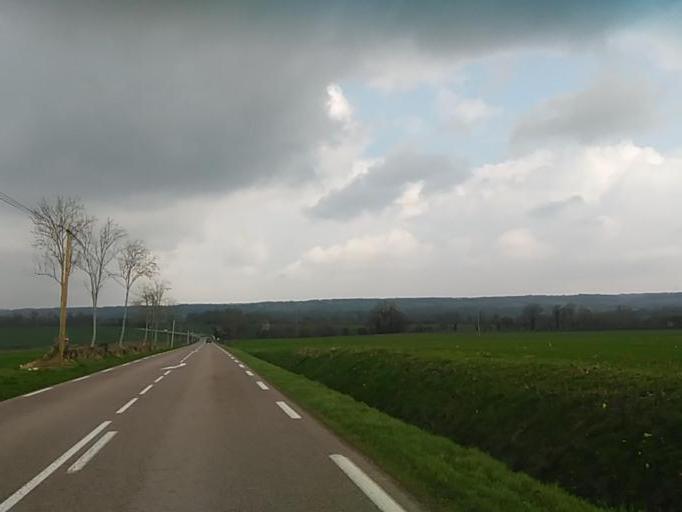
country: FR
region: Lower Normandy
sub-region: Departement de l'Orne
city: Pont-Ecrepin
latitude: 48.8280
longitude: -0.2400
